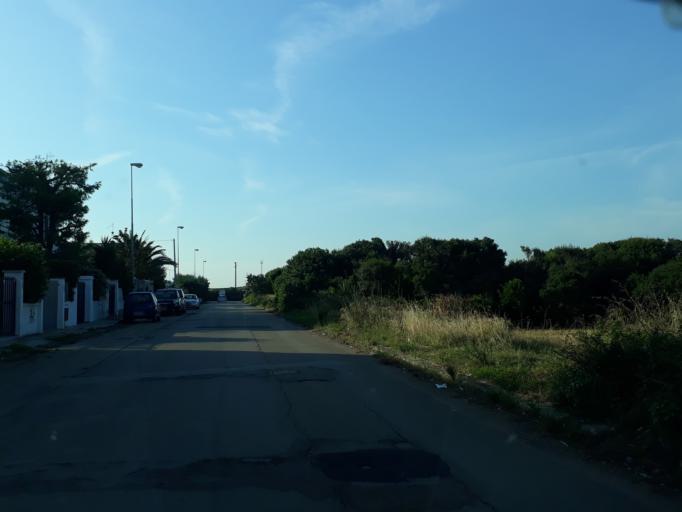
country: IT
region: Apulia
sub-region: Provincia di Brindisi
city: Carovigno
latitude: 40.7542
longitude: 17.6963
